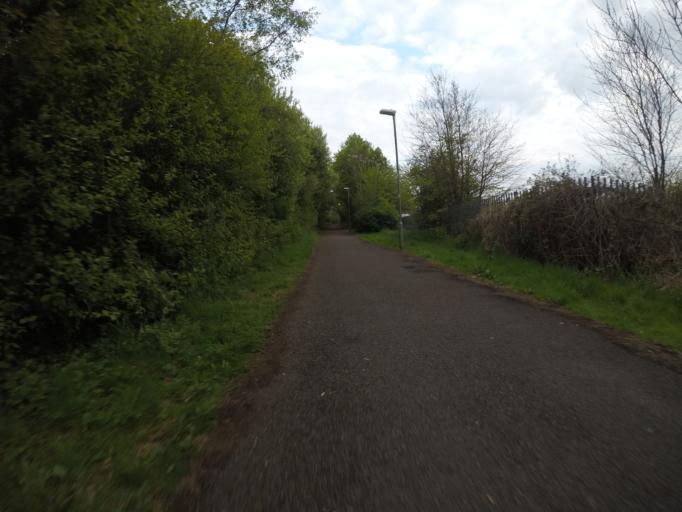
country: GB
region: Scotland
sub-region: North Ayrshire
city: Irvine
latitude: 55.6338
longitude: -4.6300
